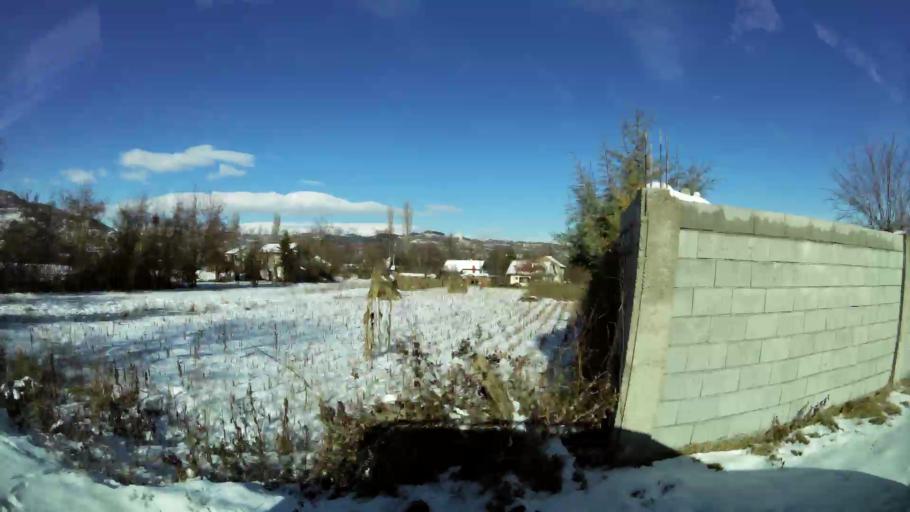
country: MK
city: Grchec
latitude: 41.9779
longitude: 21.3152
